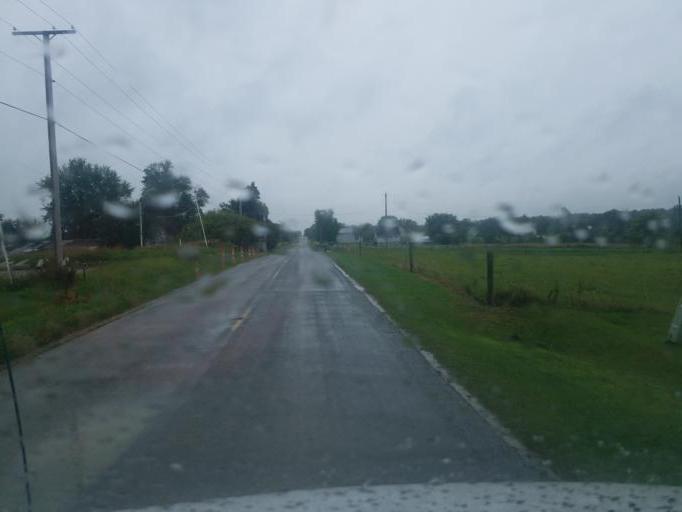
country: US
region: Ohio
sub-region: Medina County
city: Seville
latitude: 41.0373
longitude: -81.8324
